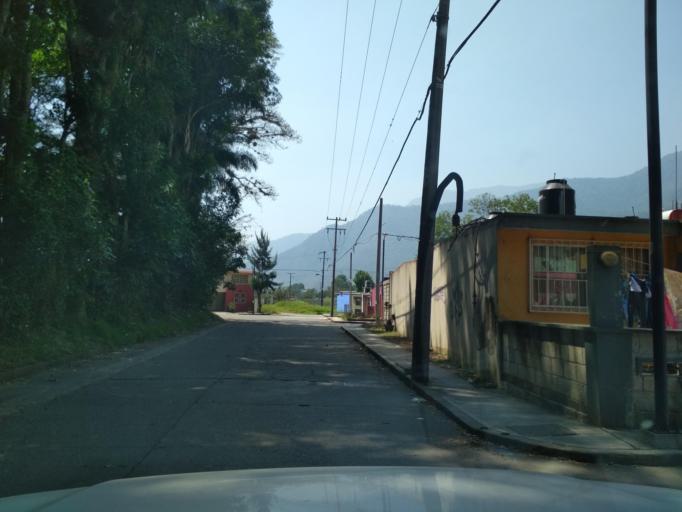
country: MX
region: Veracruz
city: Rio Blanco
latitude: 18.8451
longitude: -97.1251
